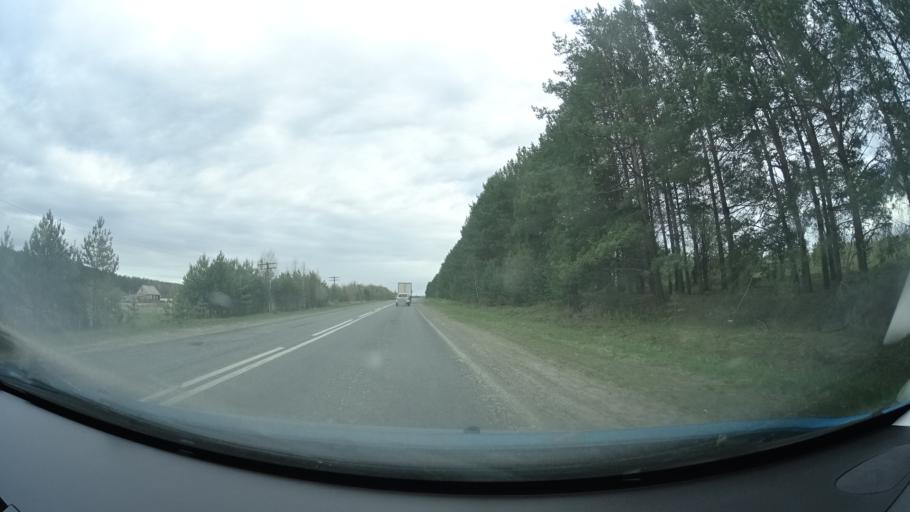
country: RU
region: Perm
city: Yugo-Kamskiy
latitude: 57.6811
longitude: 55.5738
